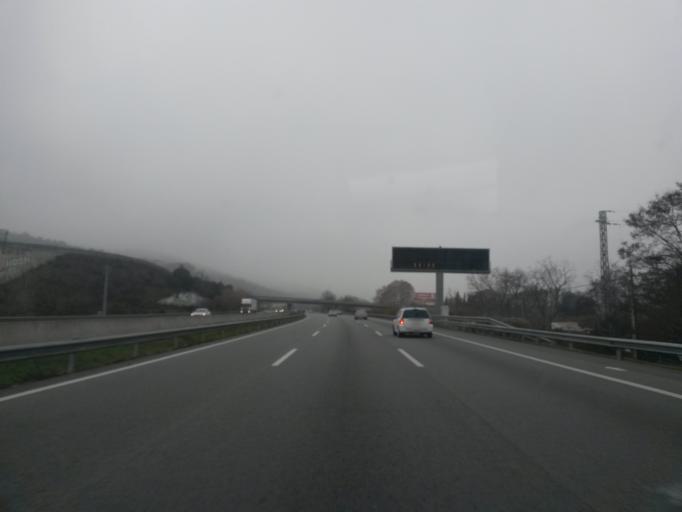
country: ES
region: Catalonia
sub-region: Provincia de Barcelona
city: Llinars del Valles
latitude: 41.6372
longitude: 2.4063
